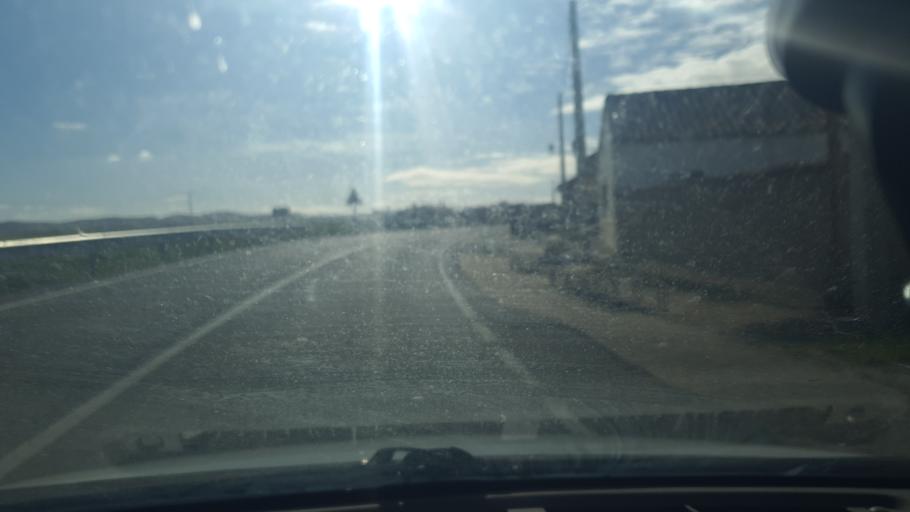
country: ES
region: Castille and Leon
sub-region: Provincia de Avila
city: Gotarrendura
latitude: 40.8251
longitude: -4.7378
